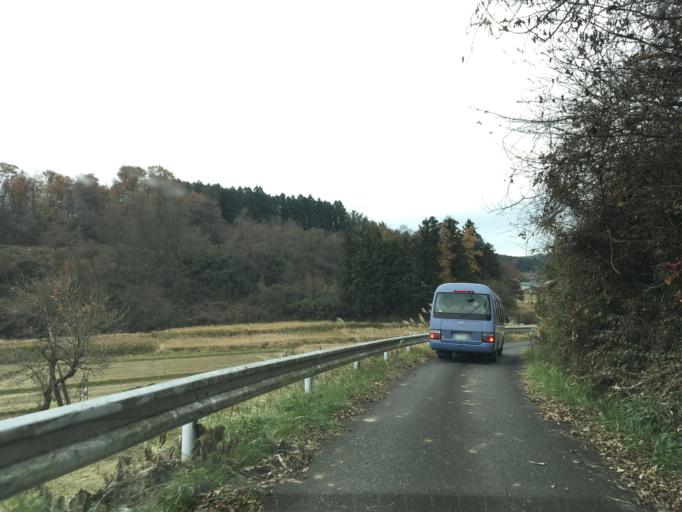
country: JP
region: Iwate
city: Ichinoseki
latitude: 38.8460
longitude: 141.0348
